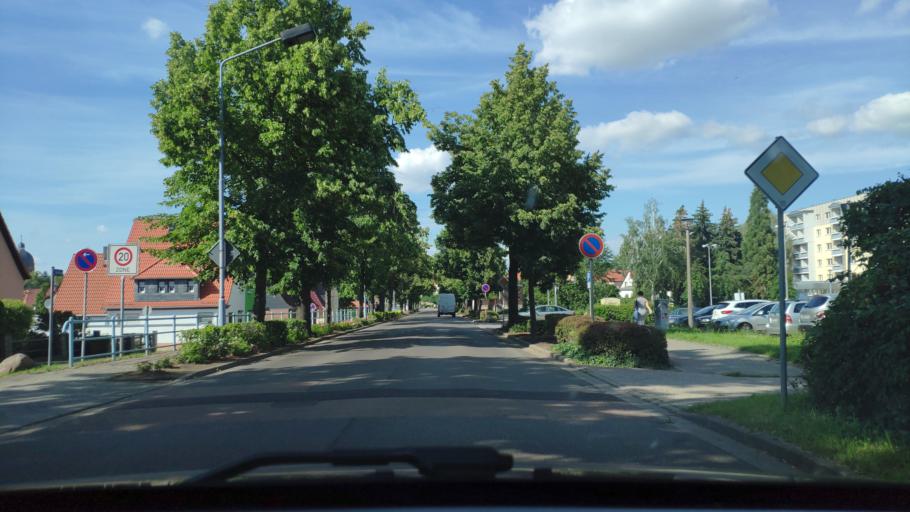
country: DE
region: Saxony-Anhalt
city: Bernburg
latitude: 51.7833
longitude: 11.7366
